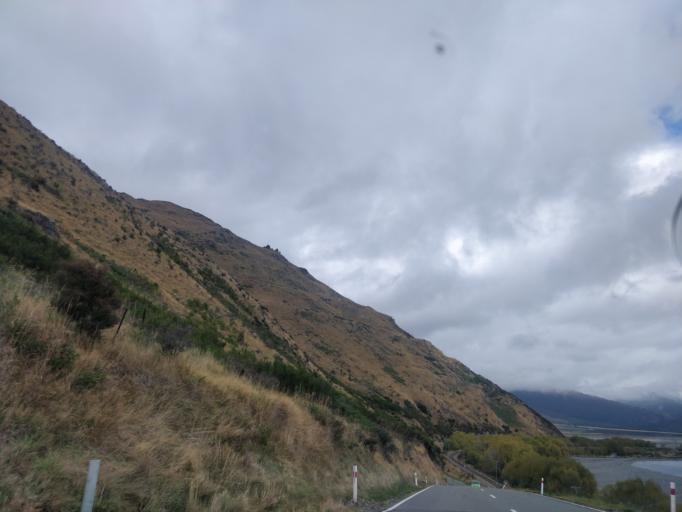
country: NZ
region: Canterbury
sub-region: Waimakariri District
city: Oxford
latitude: -43.0105
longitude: 171.7238
